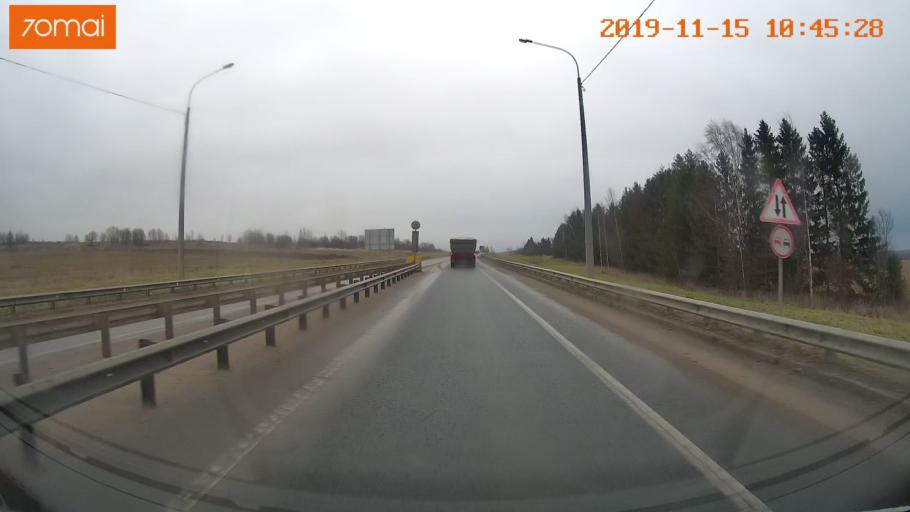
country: RU
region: Vologda
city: Sheksna
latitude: 59.2112
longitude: 38.5880
